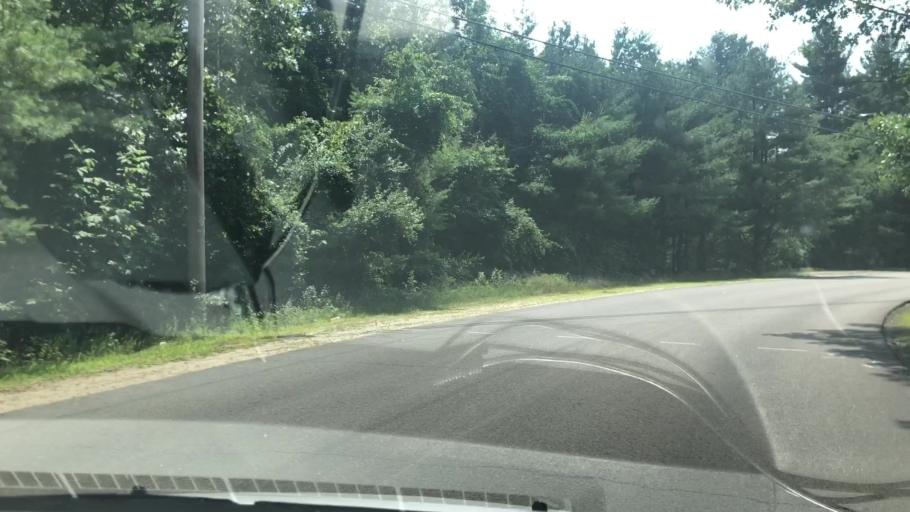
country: US
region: New Hampshire
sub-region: Hillsborough County
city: Milford
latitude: 42.8156
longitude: -71.6322
